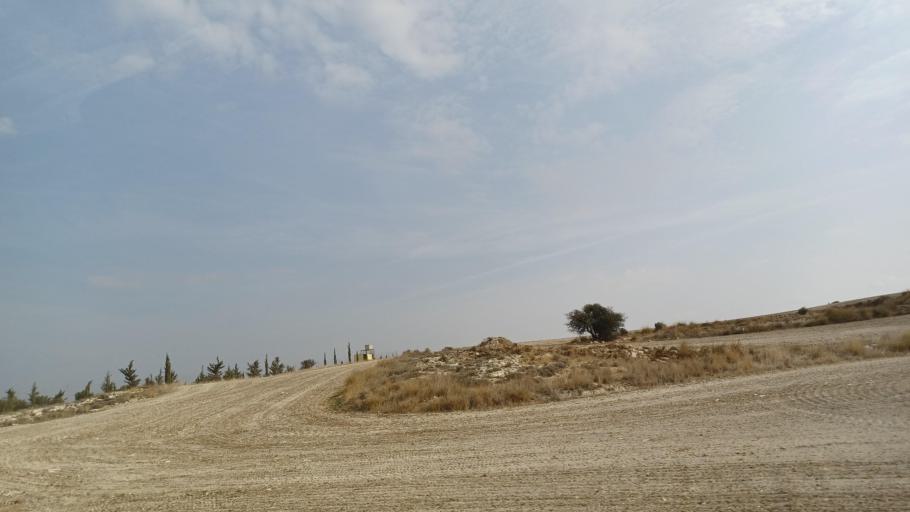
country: CY
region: Larnaka
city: Aradippou
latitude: 34.9795
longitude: 33.5798
